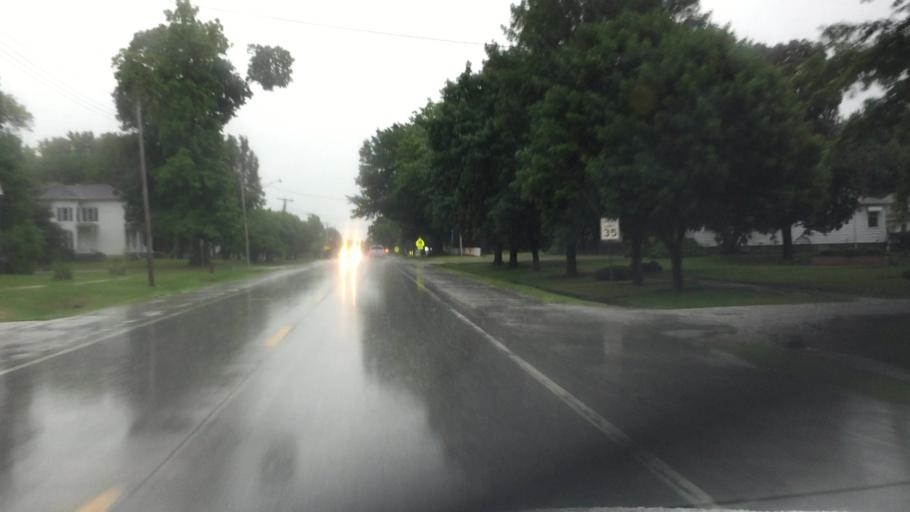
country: US
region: Illinois
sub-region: Hancock County
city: Carthage
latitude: 40.4186
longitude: -91.1362
